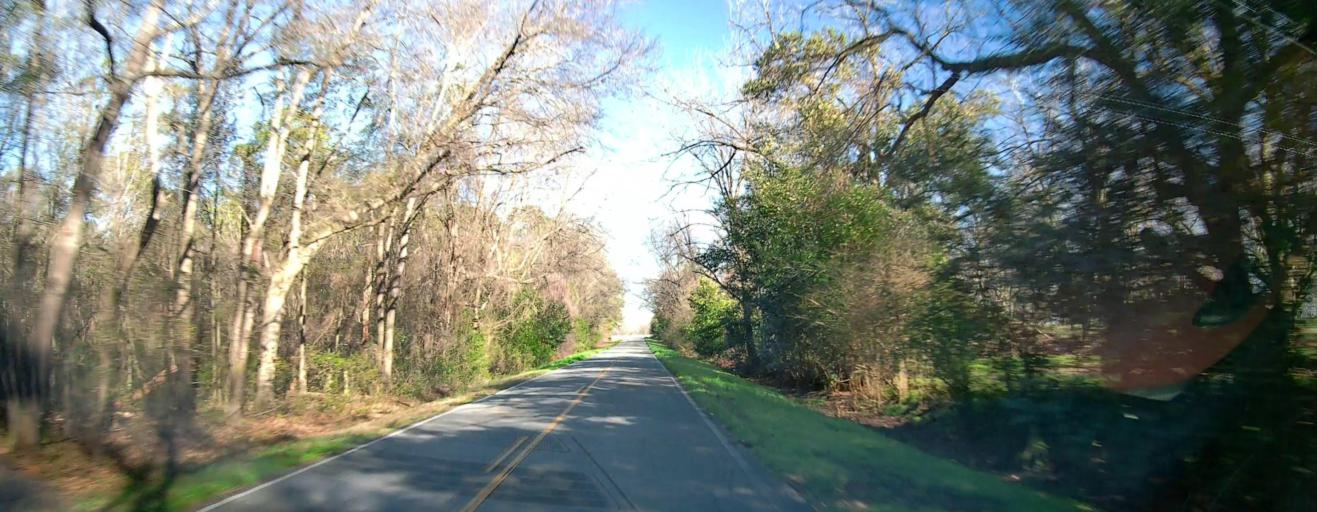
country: US
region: Georgia
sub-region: Sumter County
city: Americus
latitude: 32.0468
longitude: -84.2583
